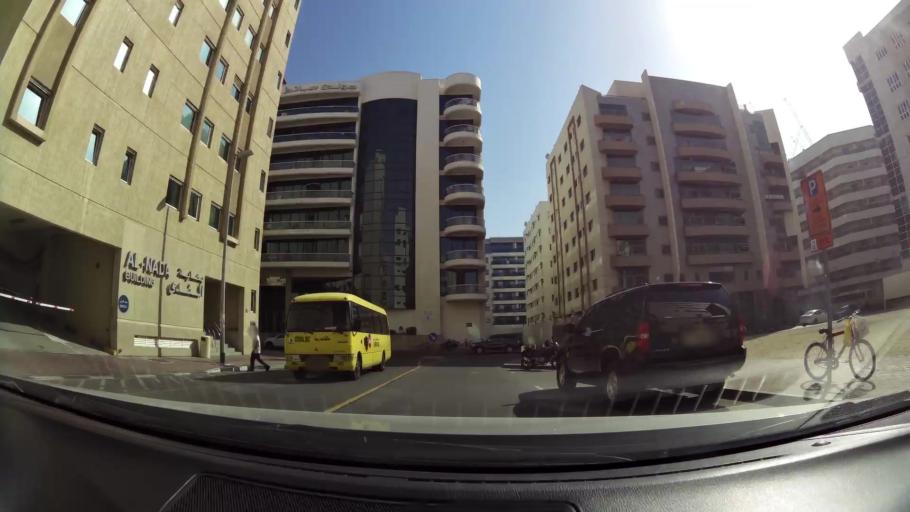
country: AE
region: Ash Shariqah
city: Sharjah
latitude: 25.2494
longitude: 55.2976
